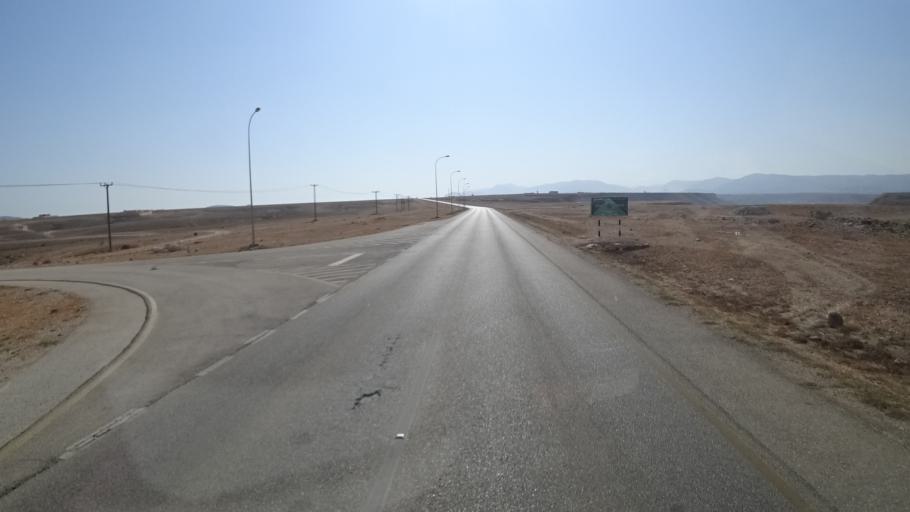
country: OM
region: Zufar
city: Salalah
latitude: 16.9508
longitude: 53.8565
